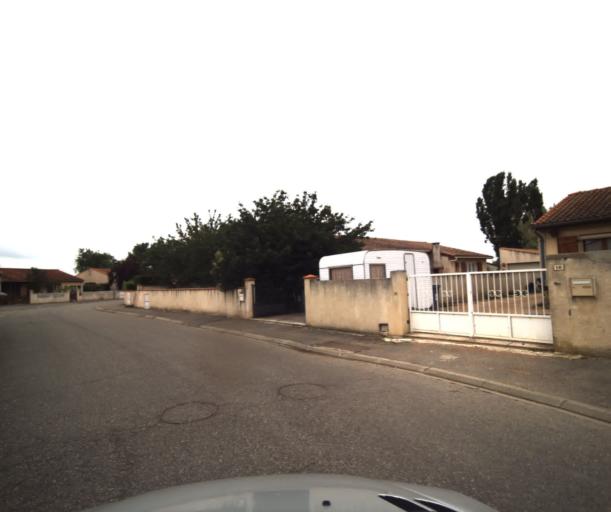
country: FR
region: Midi-Pyrenees
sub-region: Departement de la Haute-Garonne
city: Labarthe-sur-Leze
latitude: 43.4452
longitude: 1.3952
